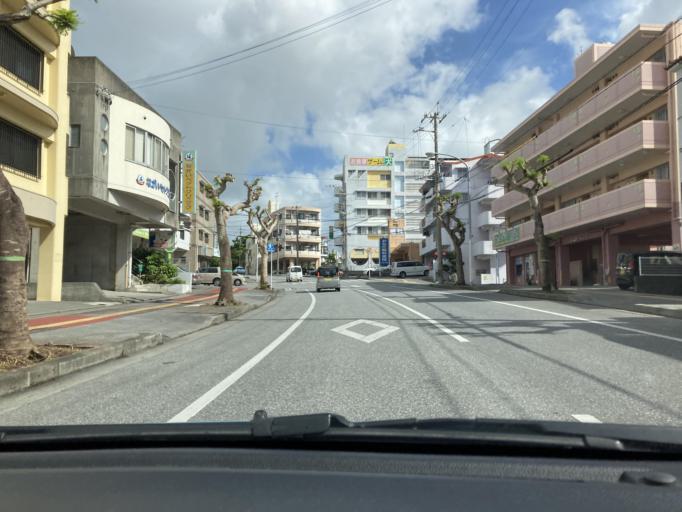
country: JP
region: Okinawa
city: Tomigusuku
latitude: 26.1829
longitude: 127.6780
